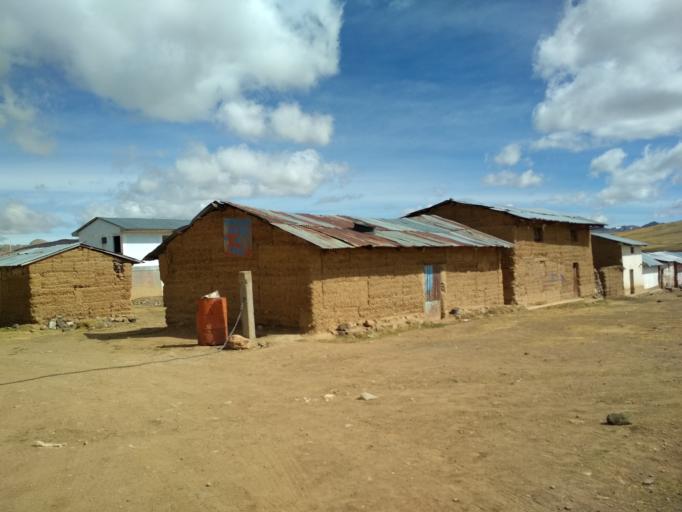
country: PE
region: Huancavelica
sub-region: Provincia de Huancavelica
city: Acobambilla
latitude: -12.7257
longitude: -75.5072
